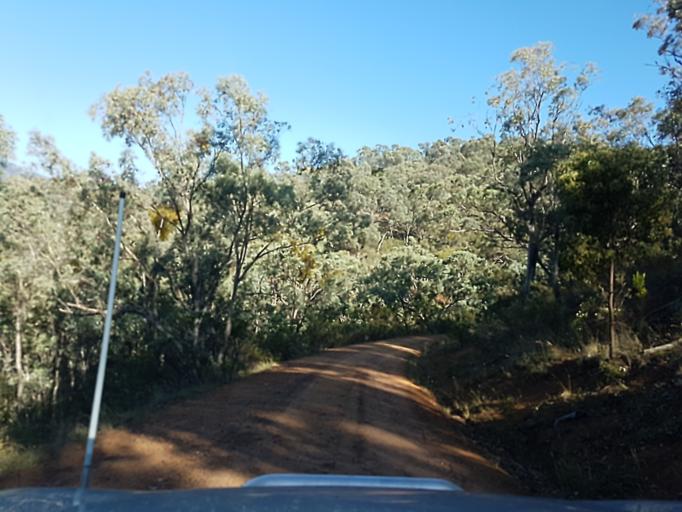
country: AU
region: New South Wales
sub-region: Snowy River
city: Jindabyne
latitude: -36.9323
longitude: 148.3356
